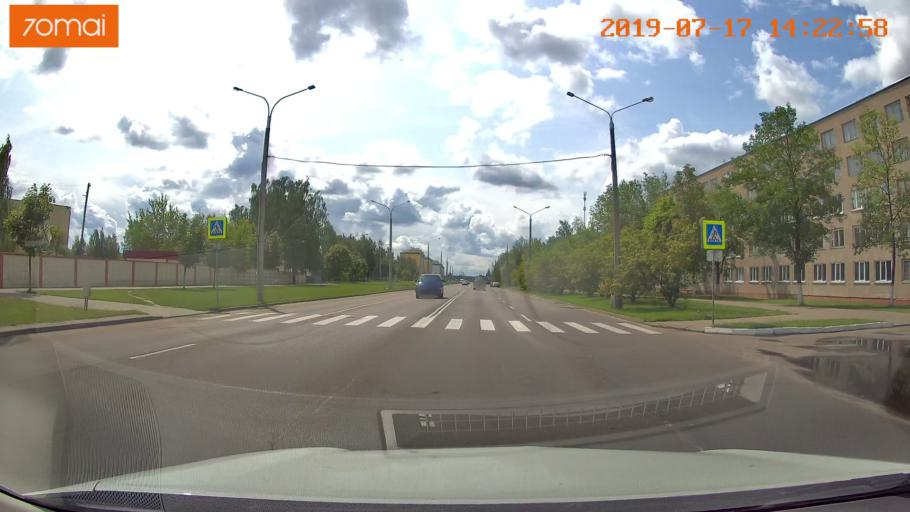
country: BY
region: Mogilev
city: Babruysk
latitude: 53.1716
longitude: 29.1768
